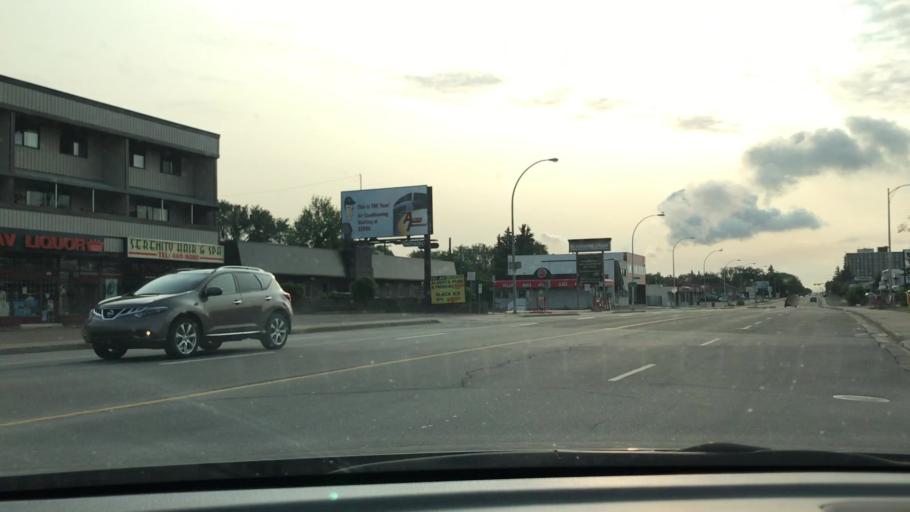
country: CA
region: Alberta
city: Edmonton
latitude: 53.5412
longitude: -113.4431
